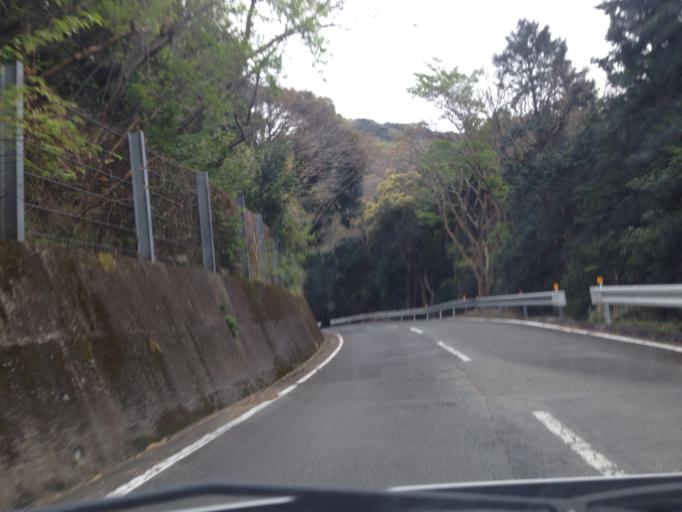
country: JP
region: Shizuoka
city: Heda
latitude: 34.9944
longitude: 138.7799
